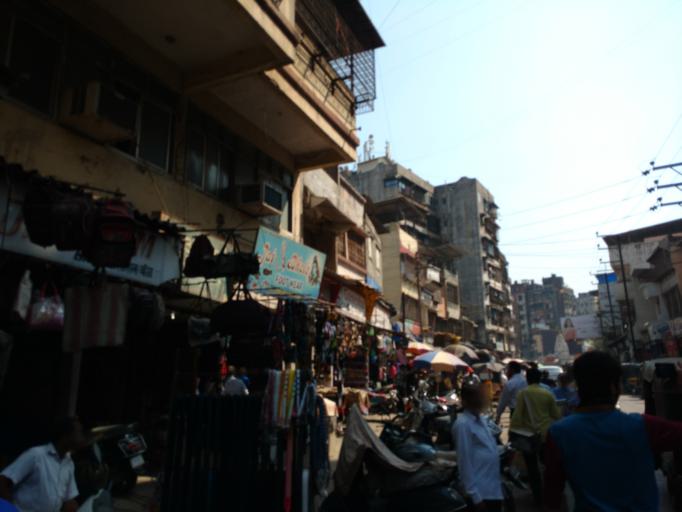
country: IN
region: Maharashtra
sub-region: Thane
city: Ulhasnagar
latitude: 19.2343
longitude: 73.1613
